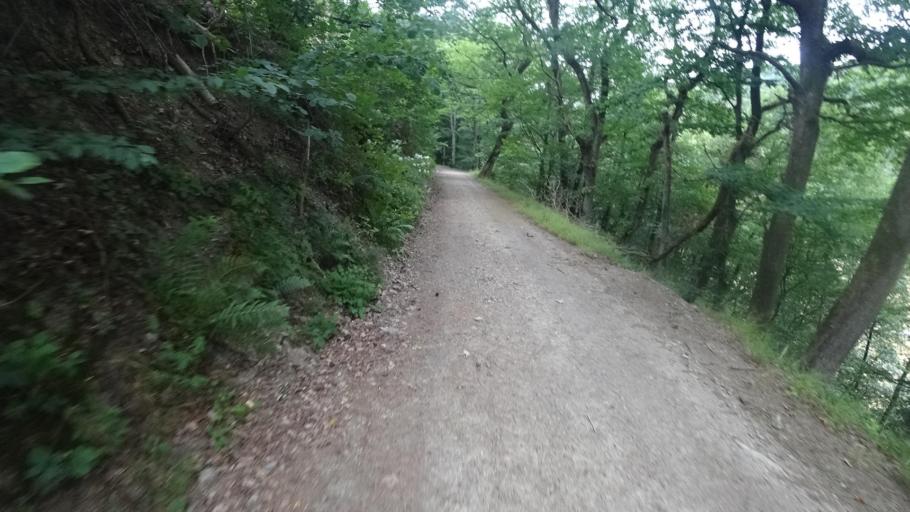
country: DE
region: Rheinland-Pfalz
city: Kesseling
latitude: 50.4825
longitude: 7.0054
